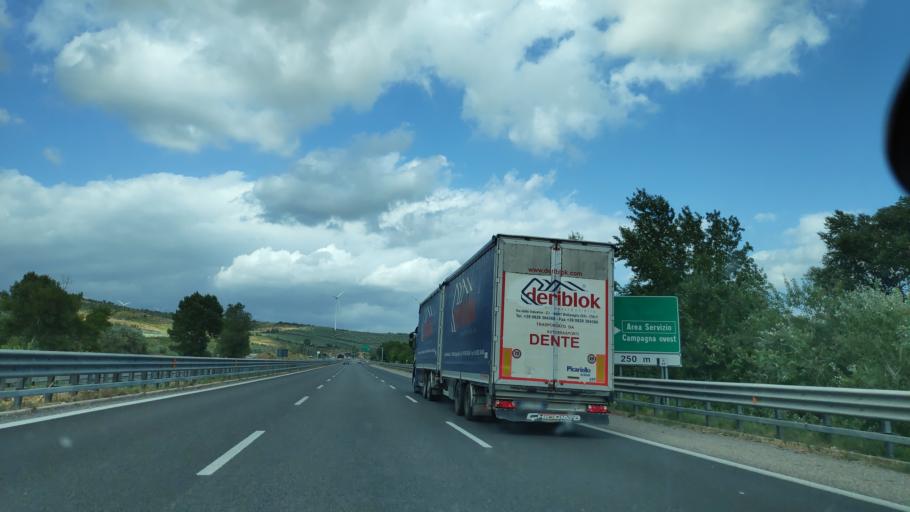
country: IT
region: Campania
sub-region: Provincia di Salerno
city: Serre
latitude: 40.6155
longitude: 15.1582
